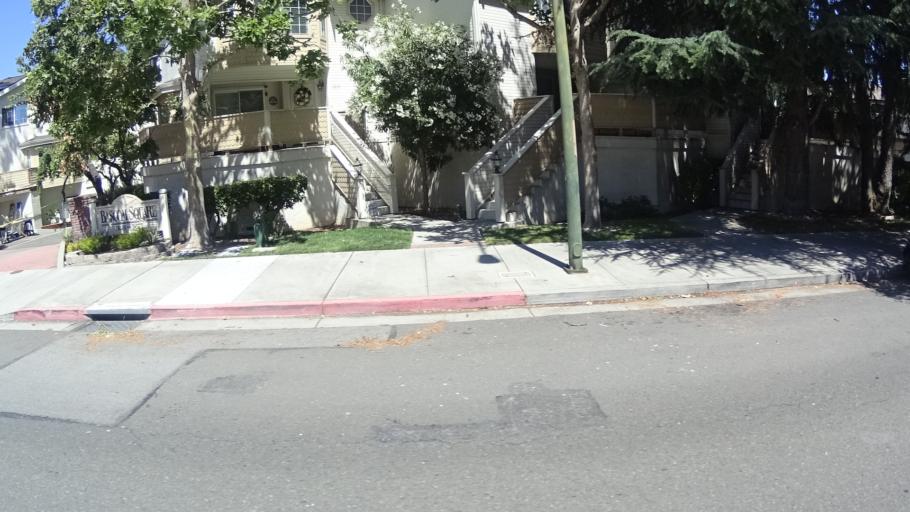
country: US
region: California
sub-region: Santa Clara County
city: Cambrian Park
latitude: 37.2614
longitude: -121.9456
